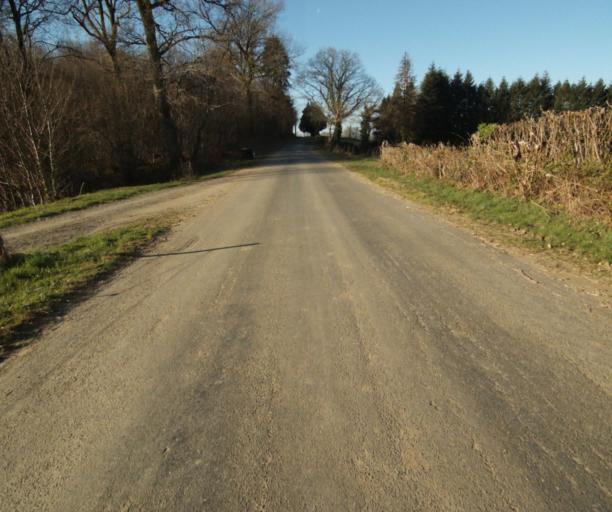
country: FR
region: Limousin
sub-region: Departement de la Correze
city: Uzerche
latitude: 45.3877
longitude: 1.5892
